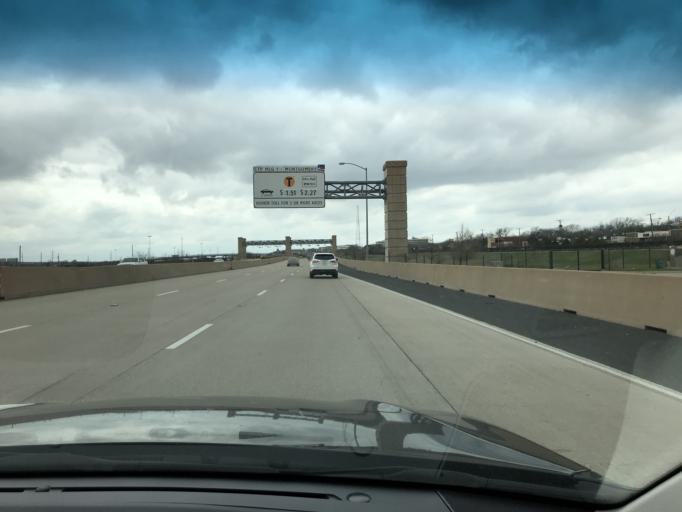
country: US
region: Texas
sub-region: Tarrant County
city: Westworth
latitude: 32.7271
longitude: -97.3751
